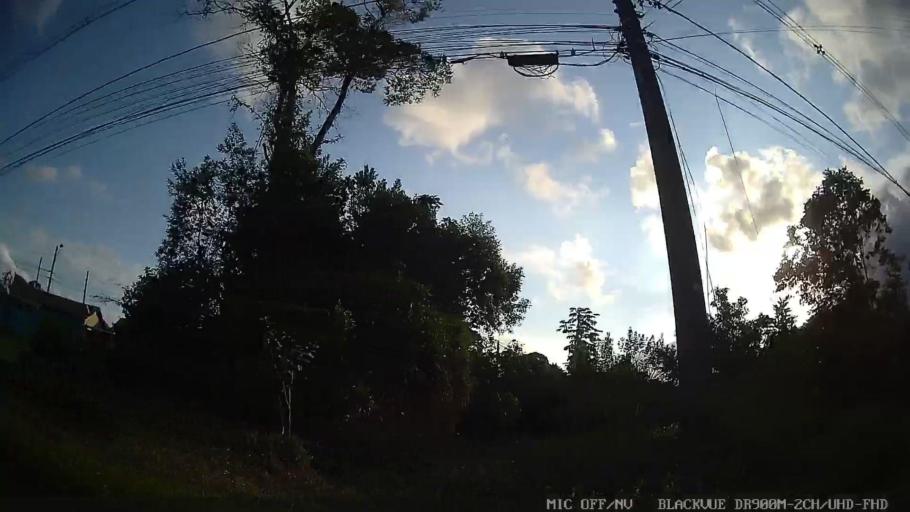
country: BR
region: Sao Paulo
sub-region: Itanhaem
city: Itanhaem
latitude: -24.1724
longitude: -46.8384
